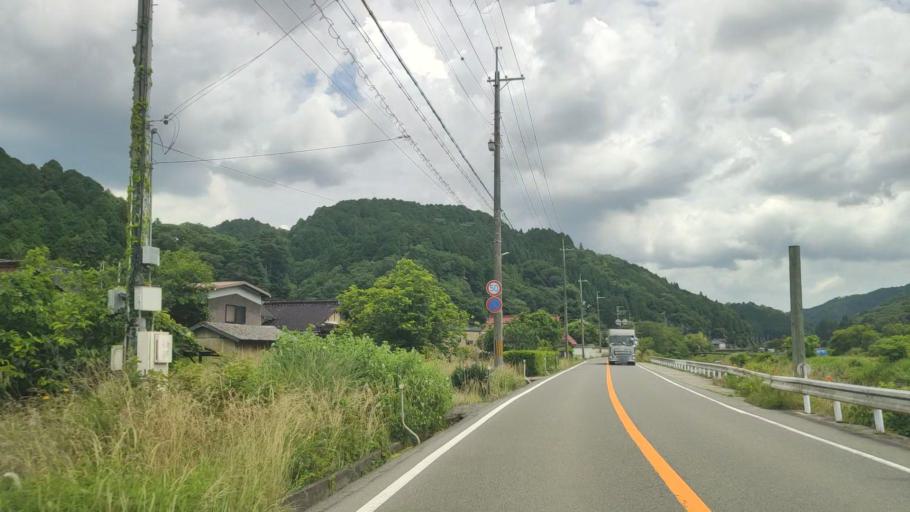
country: JP
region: Hyogo
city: Yamazakicho-nakabirose
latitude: 34.9763
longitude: 134.4450
